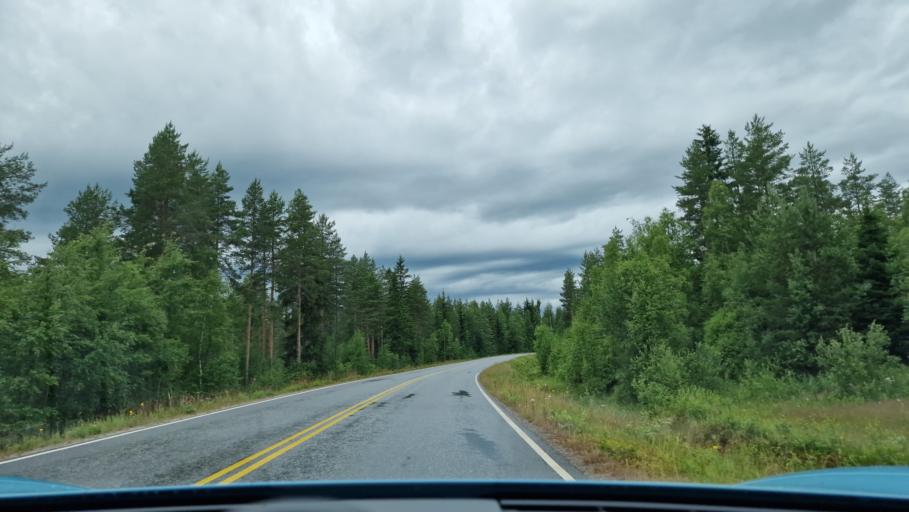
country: FI
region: Southern Ostrobothnia
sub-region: Jaerviseutu
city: Soini
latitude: 62.6841
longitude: 24.4715
